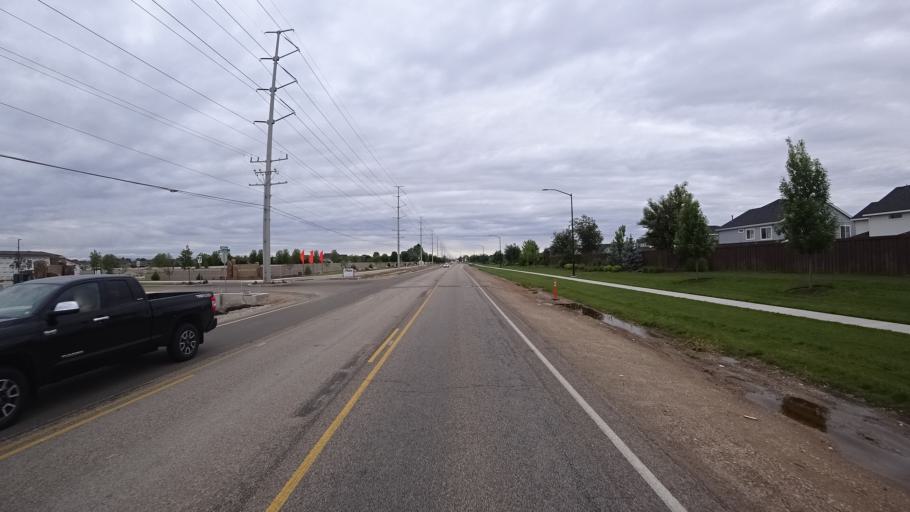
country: US
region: Idaho
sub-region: Ada County
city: Meridian
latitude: 43.6484
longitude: -116.4058
